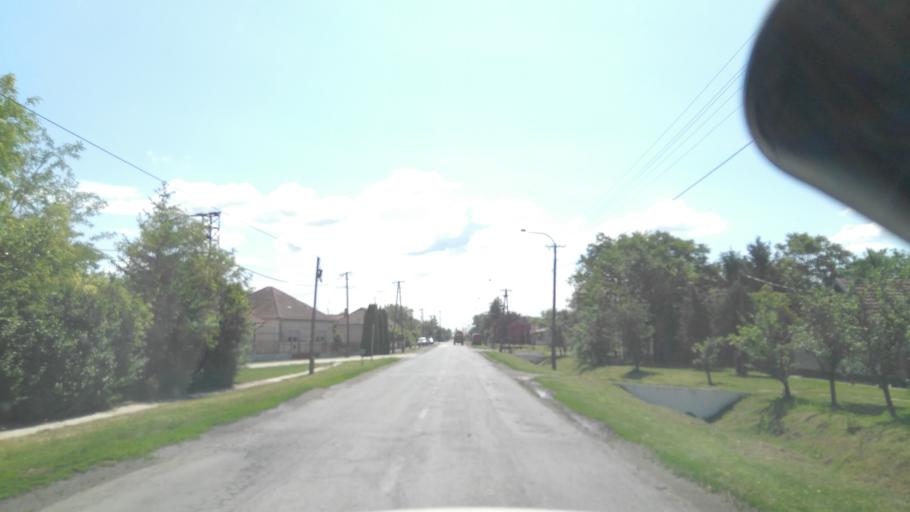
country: HU
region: Bekes
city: Kunagota
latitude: 46.4199
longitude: 21.0327
